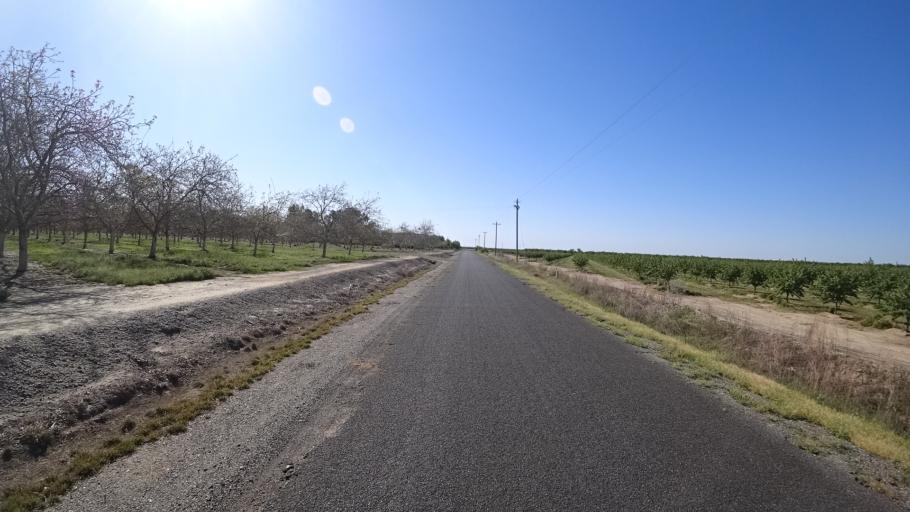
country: US
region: California
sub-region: Glenn County
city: Hamilton City
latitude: 39.7048
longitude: -122.0757
